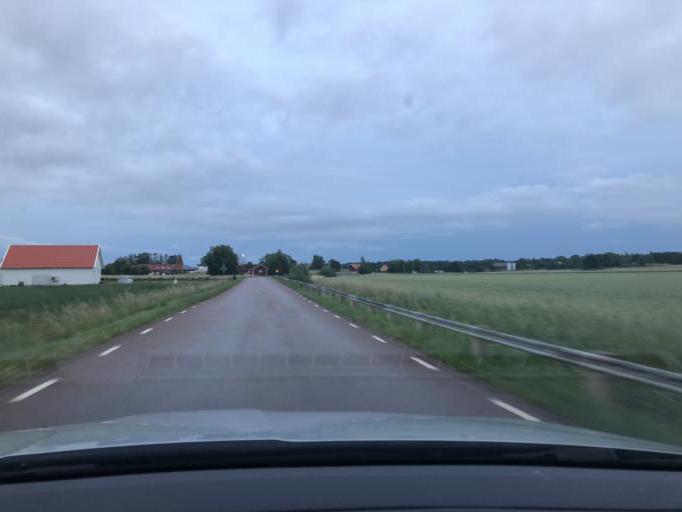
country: SE
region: OEstergoetland
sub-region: Vadstena Kommun
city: Herrestad
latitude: 58.2939
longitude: 14.7808
